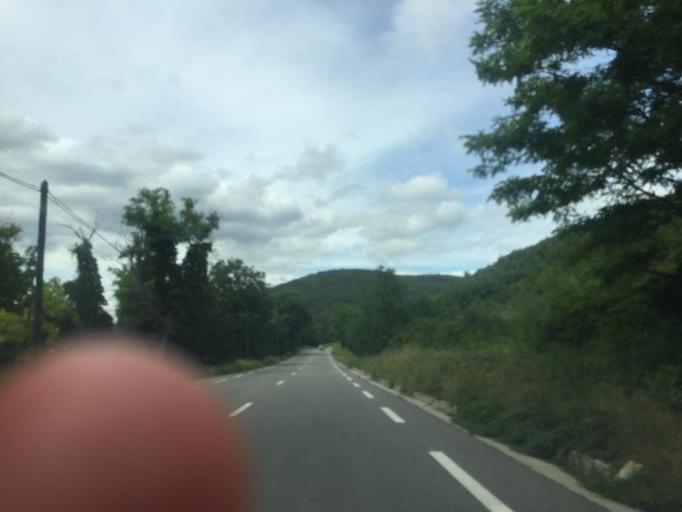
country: FR
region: Rhone-Alpes
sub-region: Departement de l'Ardeche
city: Alba-la-Romaine
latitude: 44.5110
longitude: 4.6276
